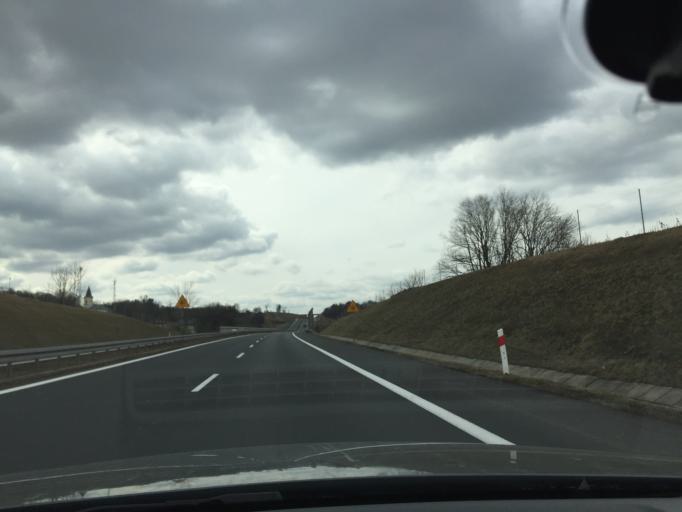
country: PL
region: Silesian Voivodeship
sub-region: Powiat cieszynski
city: Debowiec
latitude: 49.7755
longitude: 18.7237
